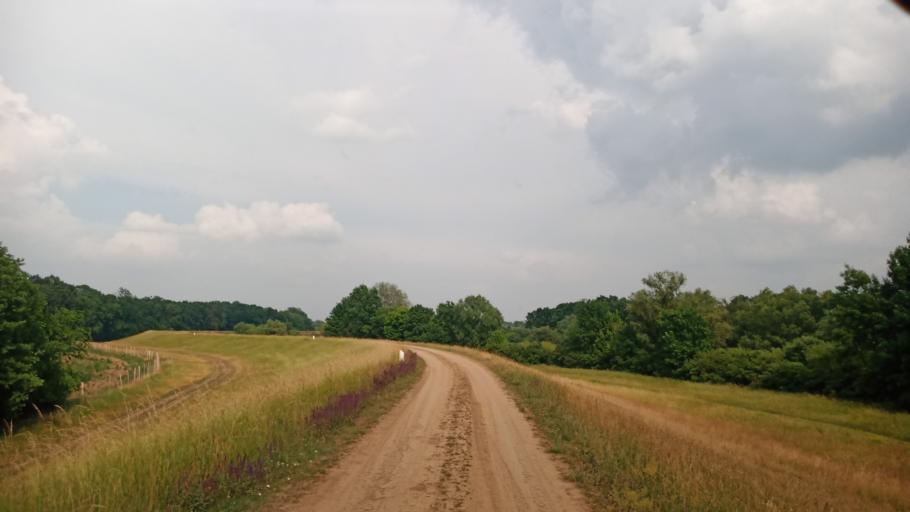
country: HU
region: Bekes
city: Doboz
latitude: 46.7062
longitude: 21.2907
